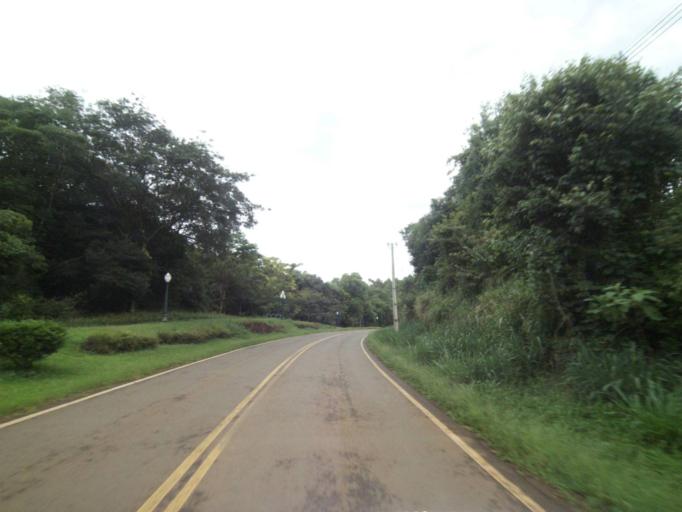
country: BR
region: Parana
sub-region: Guaraniacu
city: Guaraniacu
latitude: -25.0976
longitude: -52.8860
